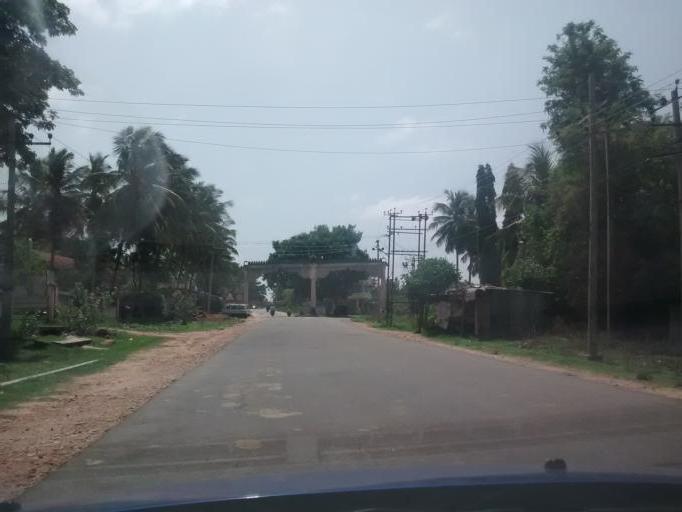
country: IN
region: Karnataka
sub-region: Hassan
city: Hole Narsipur
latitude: 12.5616
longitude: 76.2712
